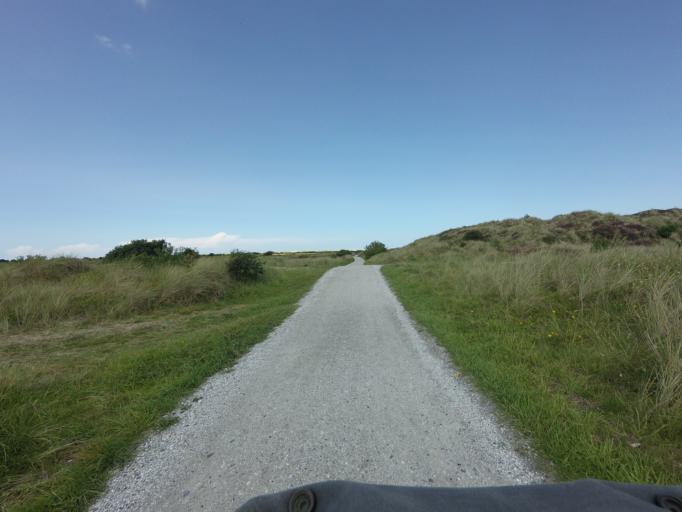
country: NL
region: Friesland
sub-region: Gemeente Terschelling
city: West-Terschelling
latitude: 53.3612
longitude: 5.2057
